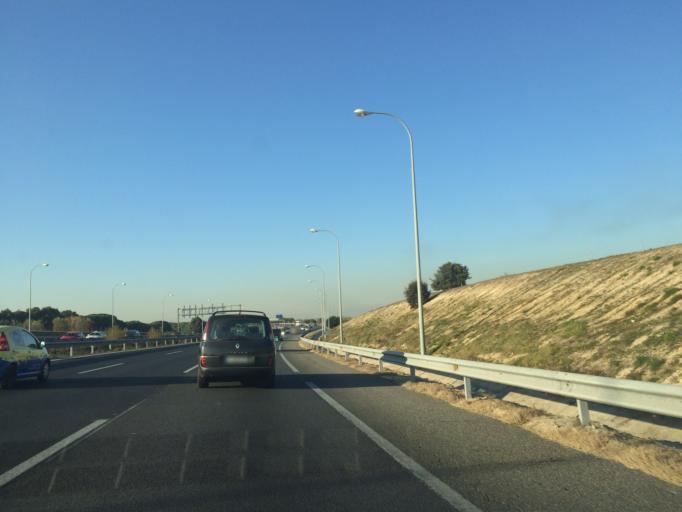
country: ES
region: Madrid
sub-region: Provincia de Madrid
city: Alcorcon
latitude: 40.3764
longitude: -3.8073
